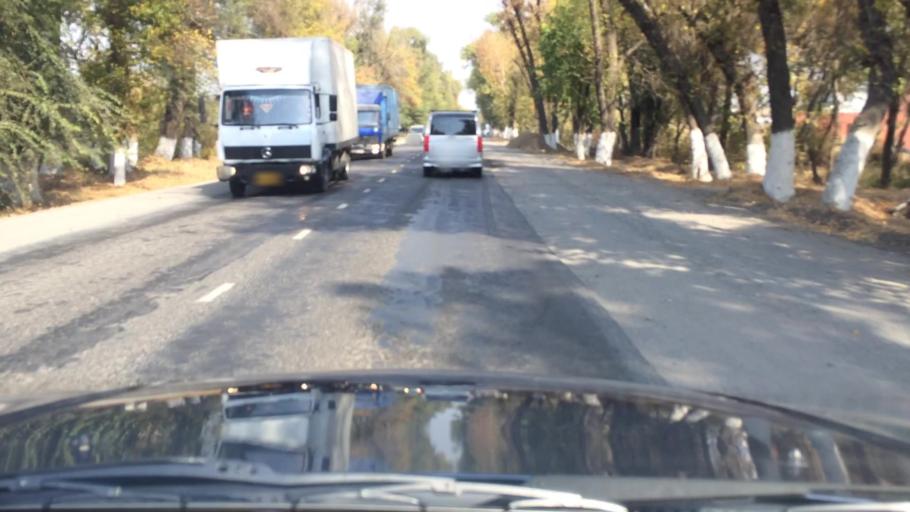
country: KG
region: Chuy
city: Lebedinovka
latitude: 42.9191
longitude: 74.6892
